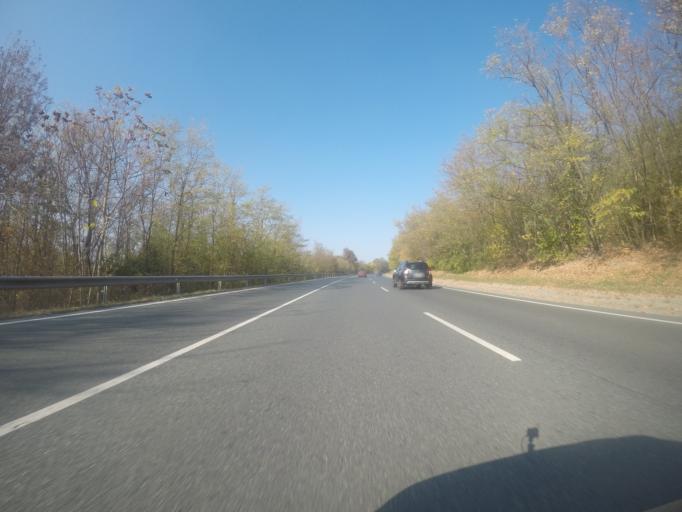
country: HU
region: Tolna
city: Madocsa
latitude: 46.6935
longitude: 18.8865
